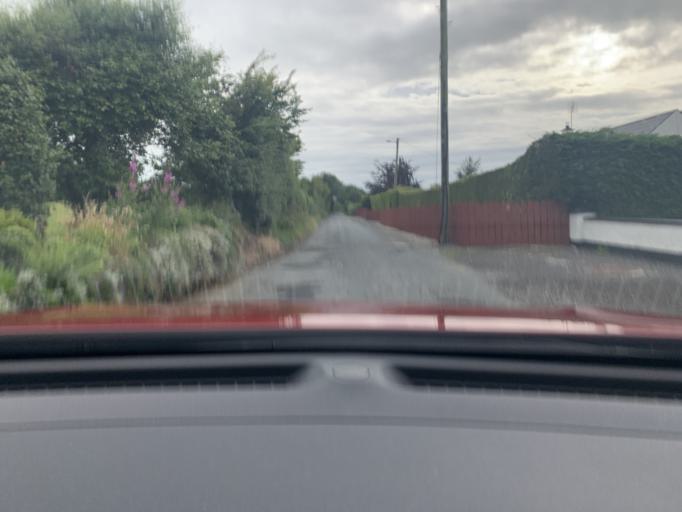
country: IE
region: Ulster
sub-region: County Donegal
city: Letterkenny
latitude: 54.9437
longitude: -7.6836
